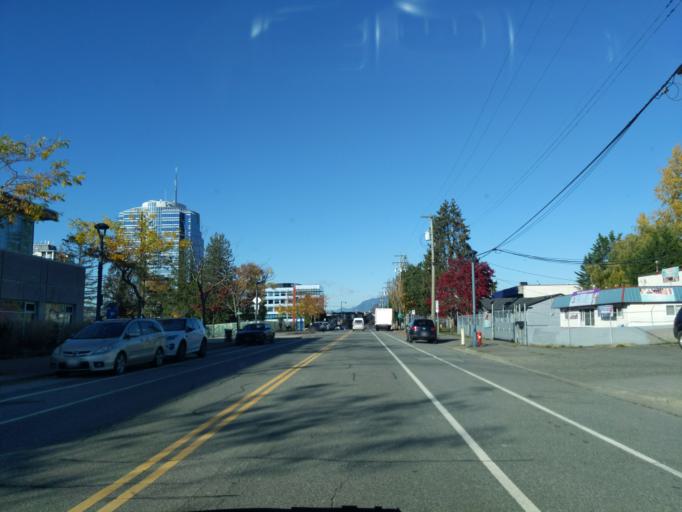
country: CA
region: British Columbia
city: New Westminster
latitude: 49.1968
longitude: -122.8488
